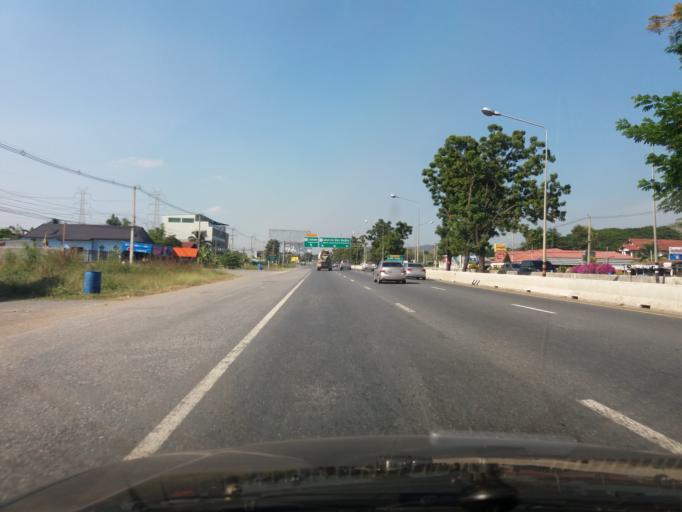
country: TH
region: Nakhon Sawan
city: Krok Phra
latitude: 15.6094
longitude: 100.1214
